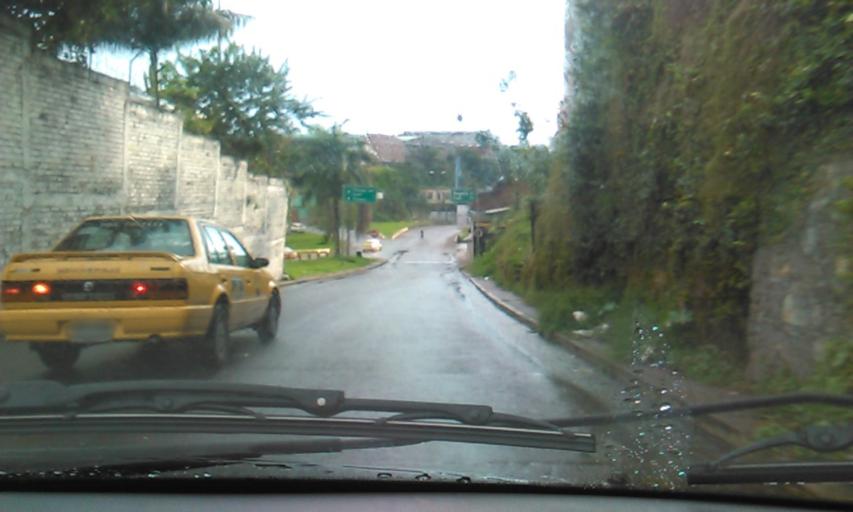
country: CO
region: Quindio
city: Armenia
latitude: 4.5342
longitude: -75.6782
